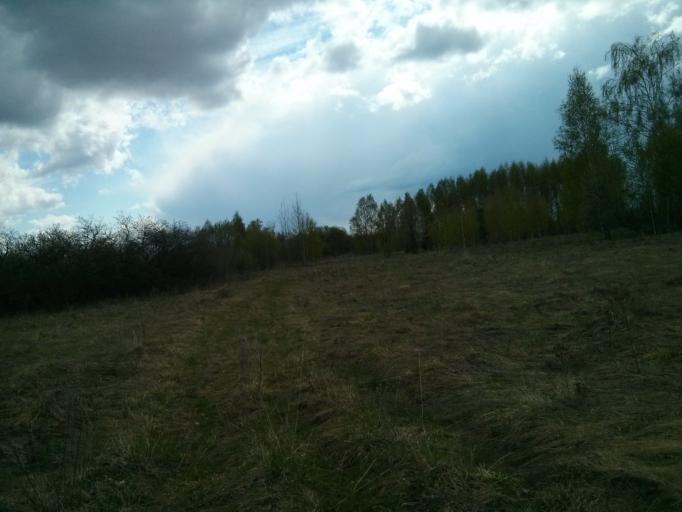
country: RU
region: Nizjnij Novgorod
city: Shimorskoye
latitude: 55.3076
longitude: 41.8444
